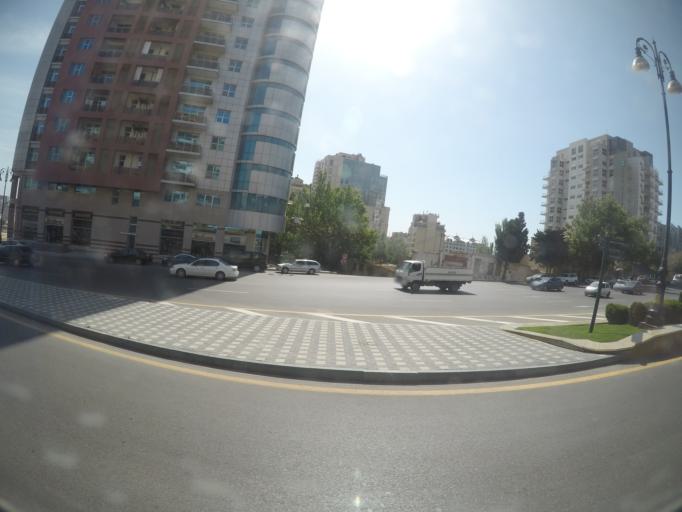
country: AZ
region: Baki
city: Badamdar
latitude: 40.3694
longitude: 49.8247
